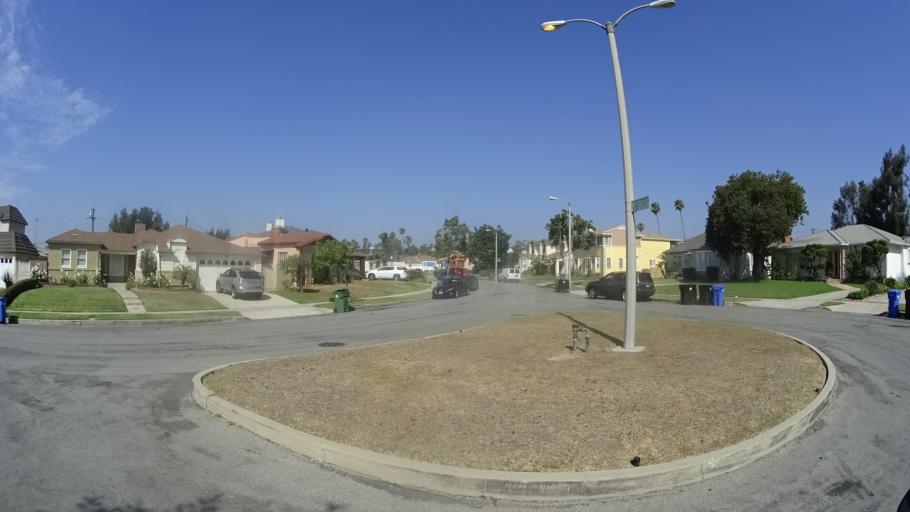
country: US
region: California
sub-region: Los Angeles County
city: View Park-Windsor Hills
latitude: 33.9920
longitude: -118.3467
